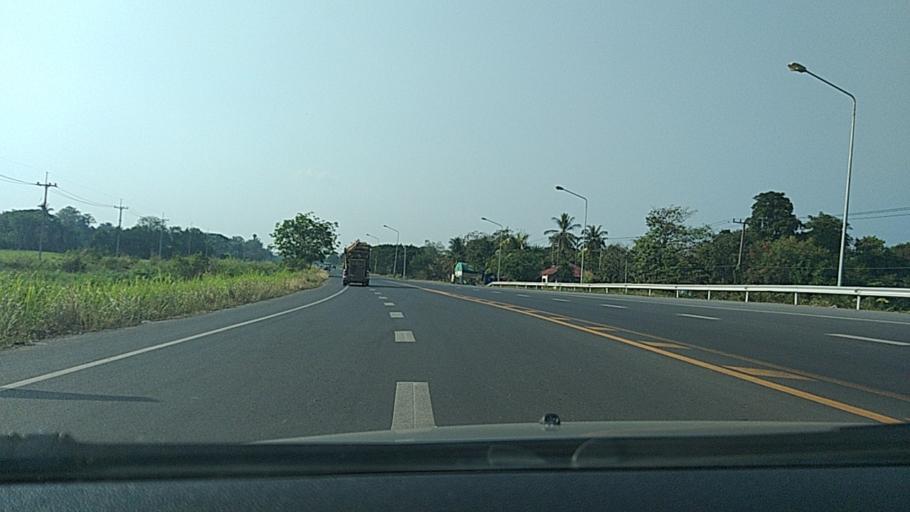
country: TH
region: Sing Buri
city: Phrom Buri
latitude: 14.7968
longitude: 100.4429
